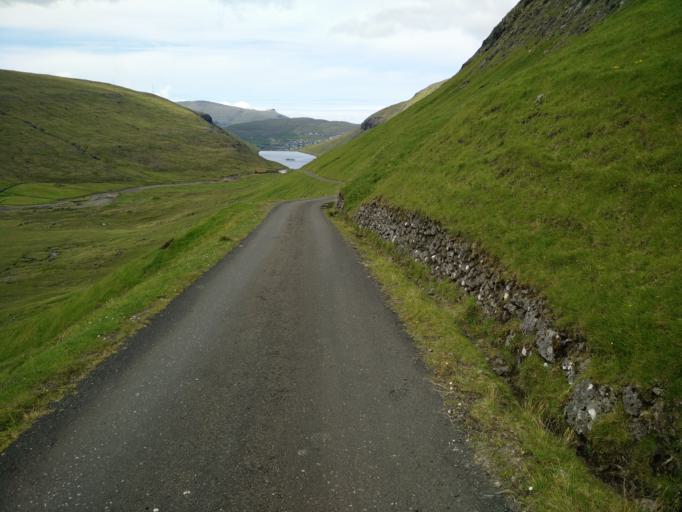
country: FO
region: Streymoy
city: Vestmanna
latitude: 62.1544
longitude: -7.0844
